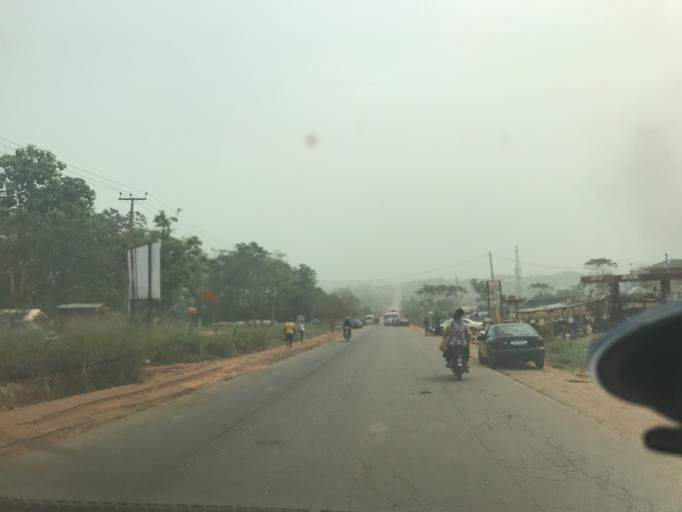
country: NG
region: Ogun
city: Ilaro
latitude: 6.8968
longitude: 3.0243
